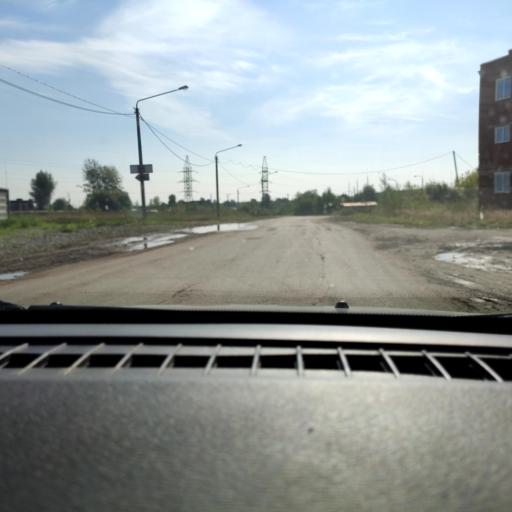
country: RU
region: Perm
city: Novyye Lyady
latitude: 58.0549
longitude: 56.5914
